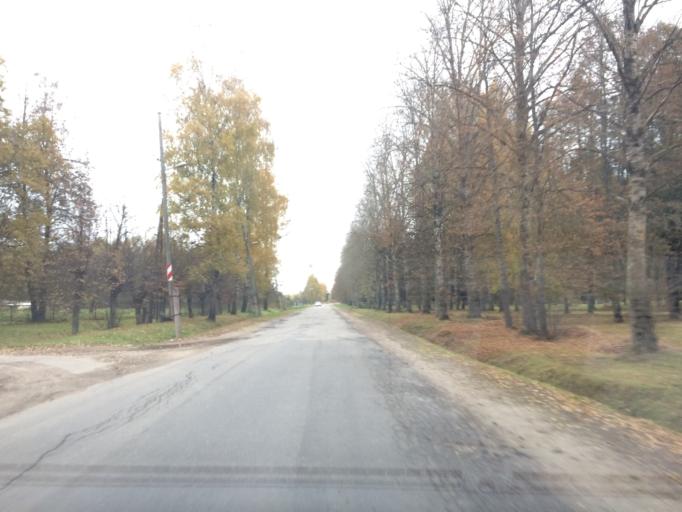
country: LV
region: Plavinu
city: Plavinas
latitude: 56.6178
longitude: 25.7566
